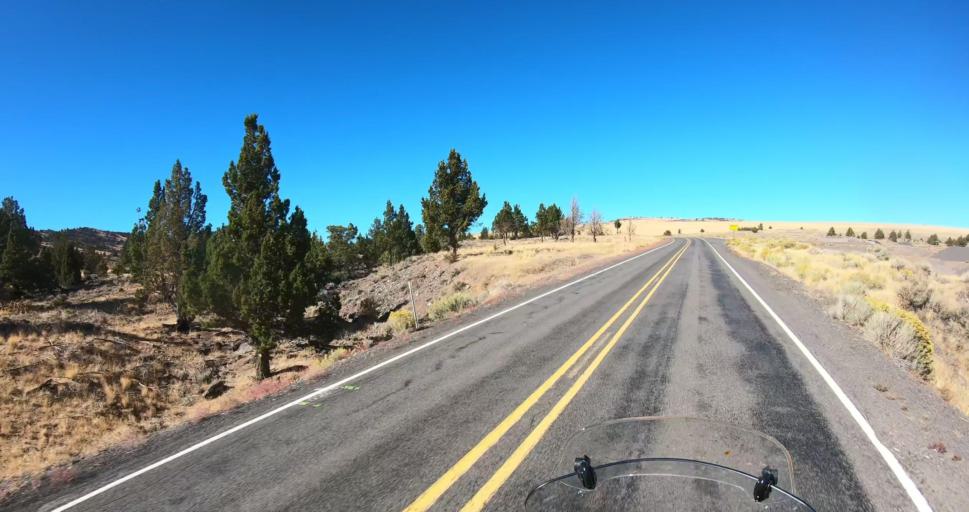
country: US
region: Oregon
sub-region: Lake County
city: Lakeview
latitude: 43.0128
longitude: -120.7727
